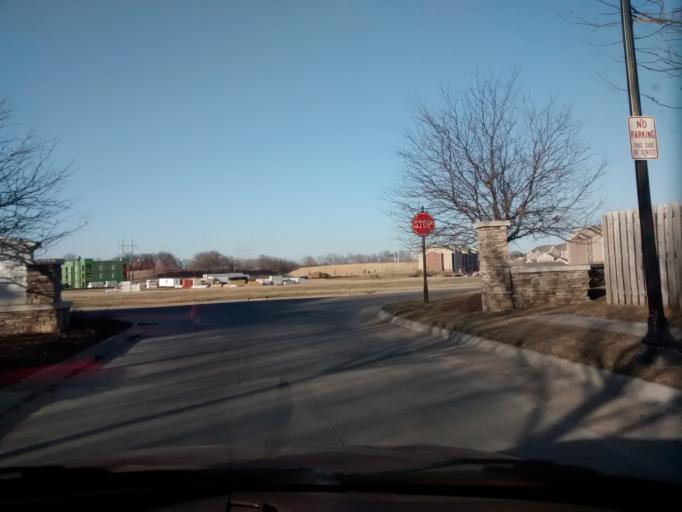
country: US
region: Nebraska
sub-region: Sarpy County
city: Offutt Air Force Base
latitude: 41.1447
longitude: -95.9781
